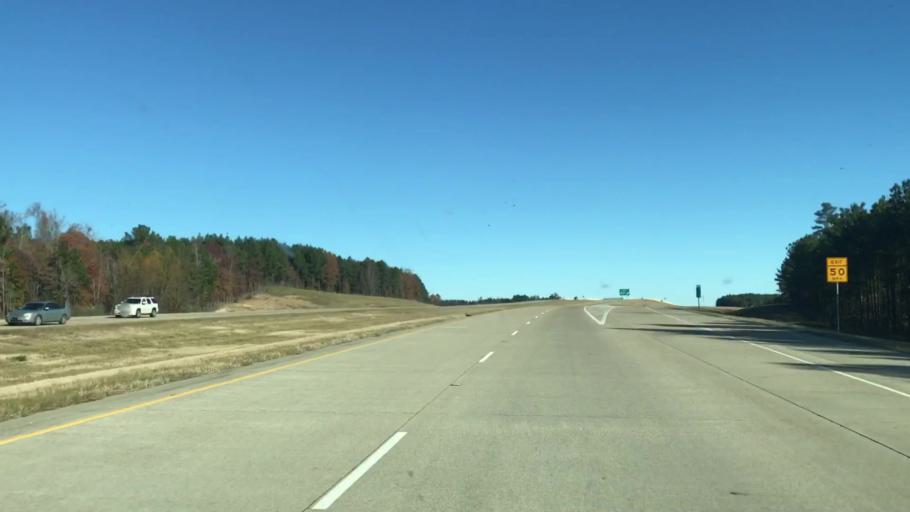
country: US
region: Louisiana
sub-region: Caddo Parish
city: Oil City
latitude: 32.8094
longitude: -93.8845
